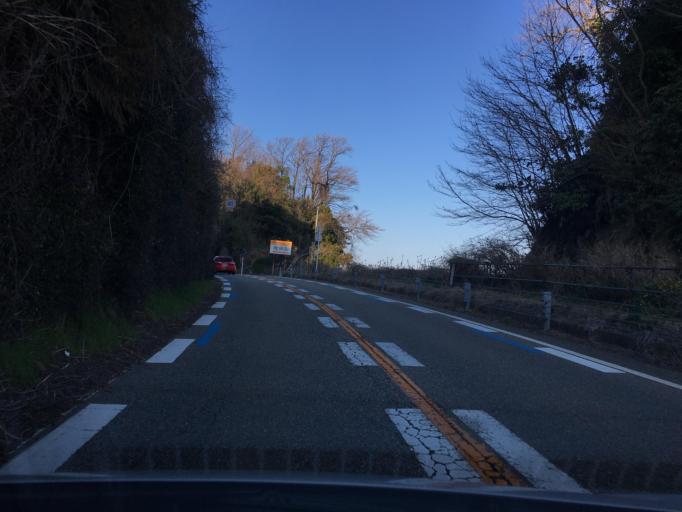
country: JP
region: Toyama
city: Himi
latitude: 36.9076
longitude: 137.0159
